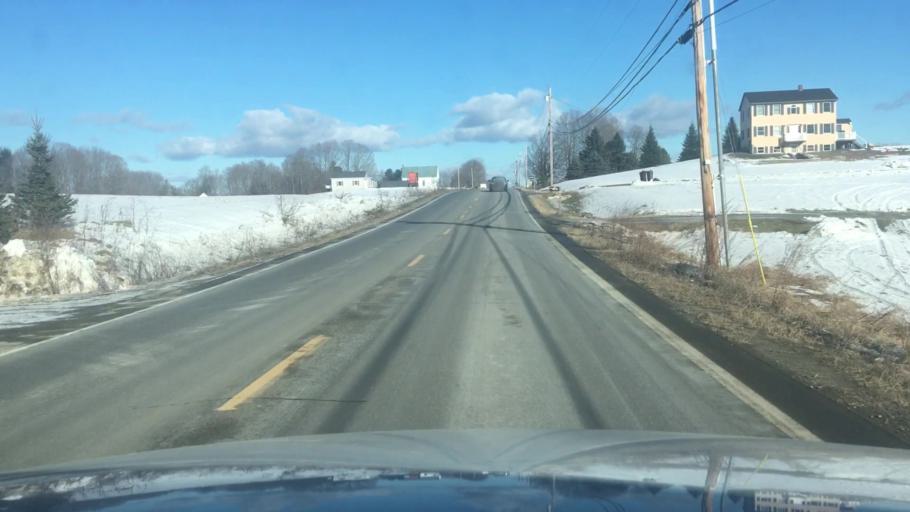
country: US
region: Maine
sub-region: Somerset County
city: Fairfield
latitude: 44.6356
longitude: -69.6802
